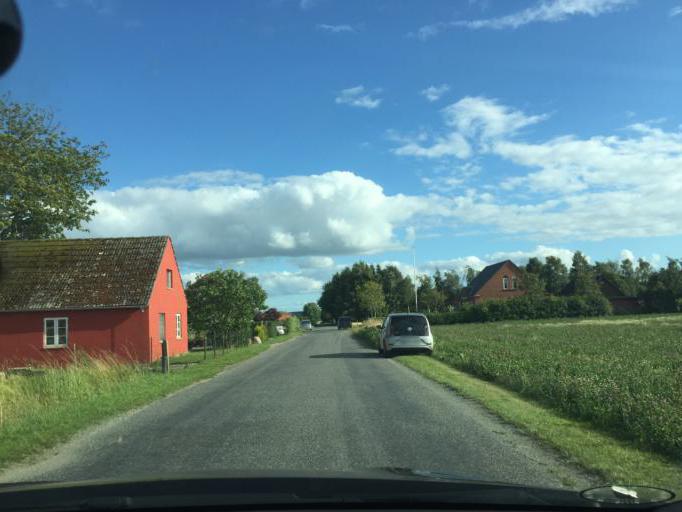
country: DK
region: South Denmark
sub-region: Faaborg-Midtfyn Kommune
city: Arslev
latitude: 55.2910
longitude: 10.5399
